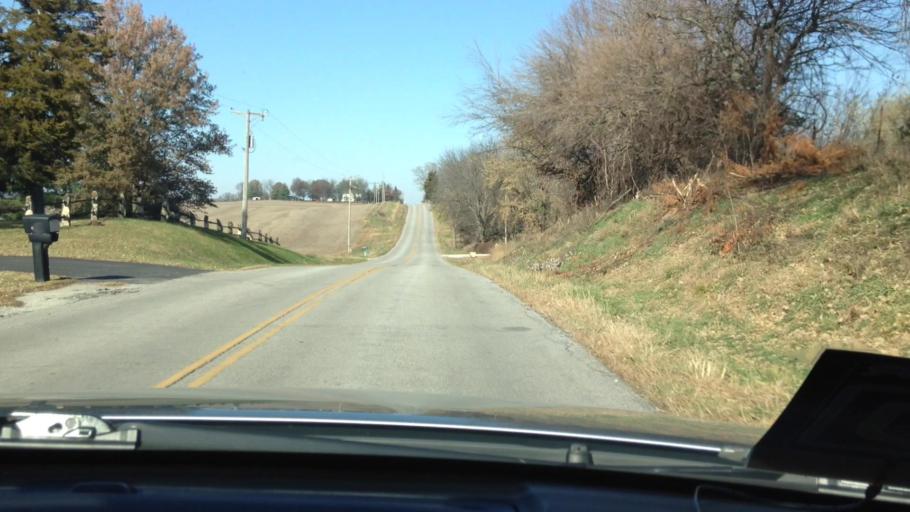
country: US
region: Missouri
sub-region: Platte County
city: Weston
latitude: 39.4354
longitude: -94.8541
